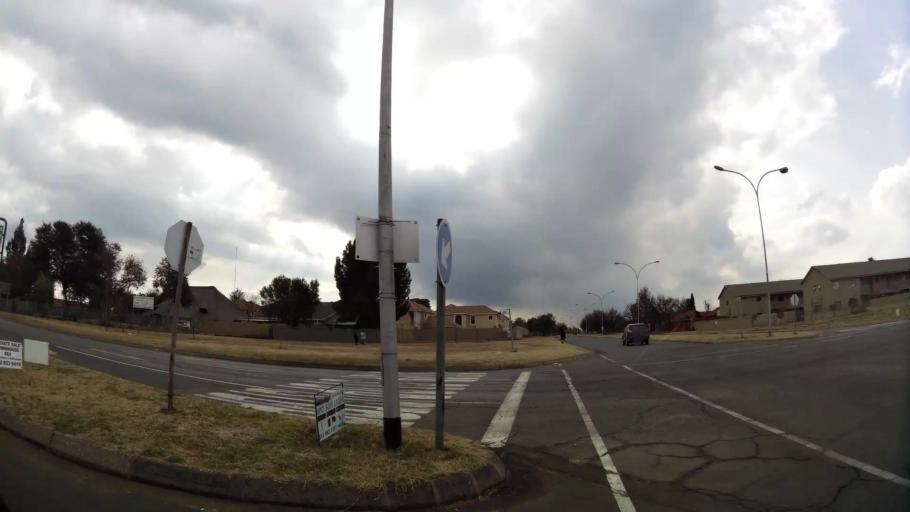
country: ZA
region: Gauteng
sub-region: Sedibeng District Municipality
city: Vanderbijlpark
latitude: -26.7307
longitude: 27.8535
